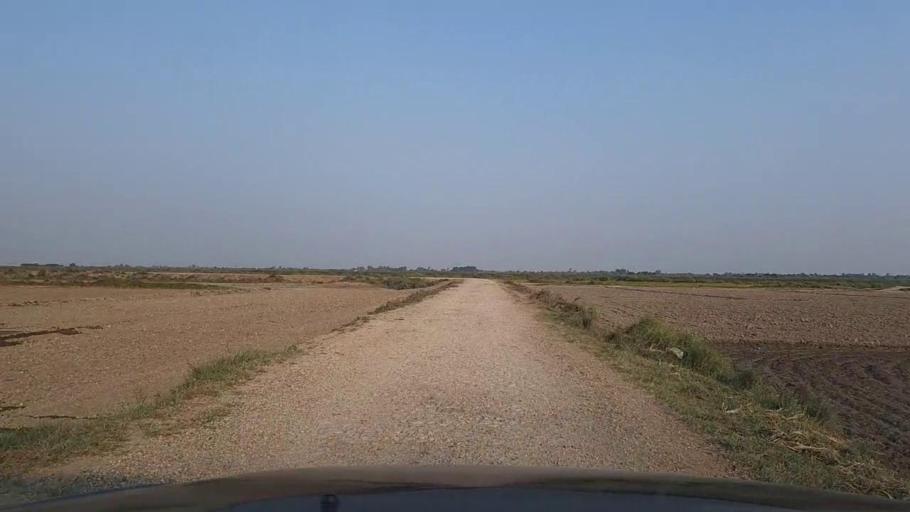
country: PK
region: Sindh
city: Mirpur Sakro
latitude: 24.4112
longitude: 67.7309
